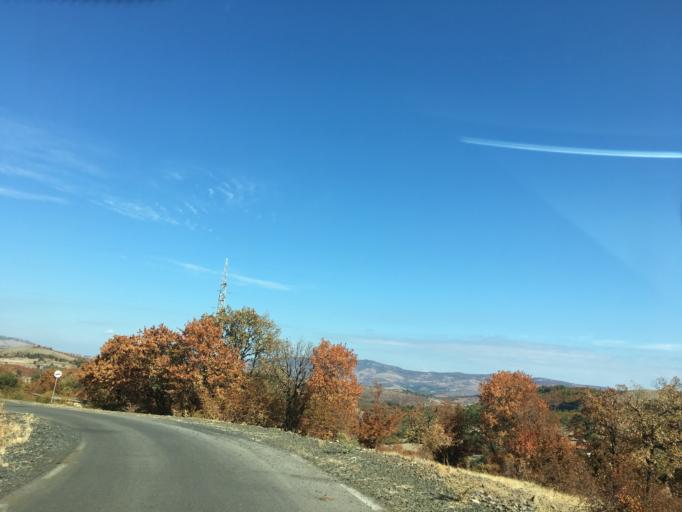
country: BG
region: Kurdzhali
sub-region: Obshtina Krumovgrad
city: Krumovgrad
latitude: 41.4922
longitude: 25.5282
